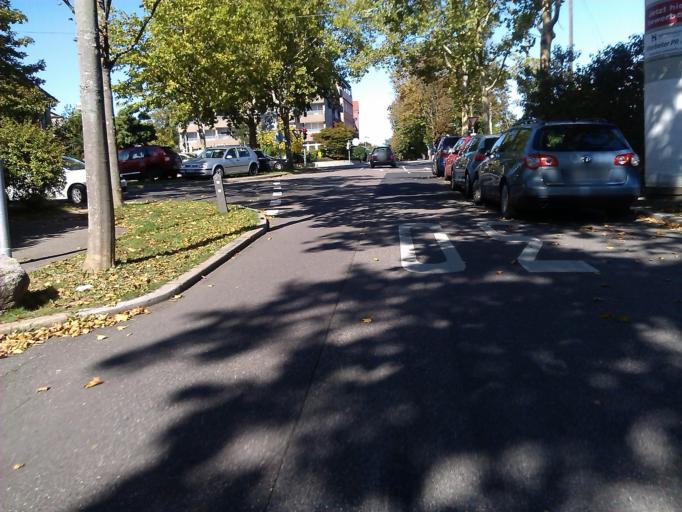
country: DE
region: Baden-Wuerttemberg
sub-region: Regierungsbezirk Stuttgart
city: Heilbronn
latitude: 49.1473
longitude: 9.2328
